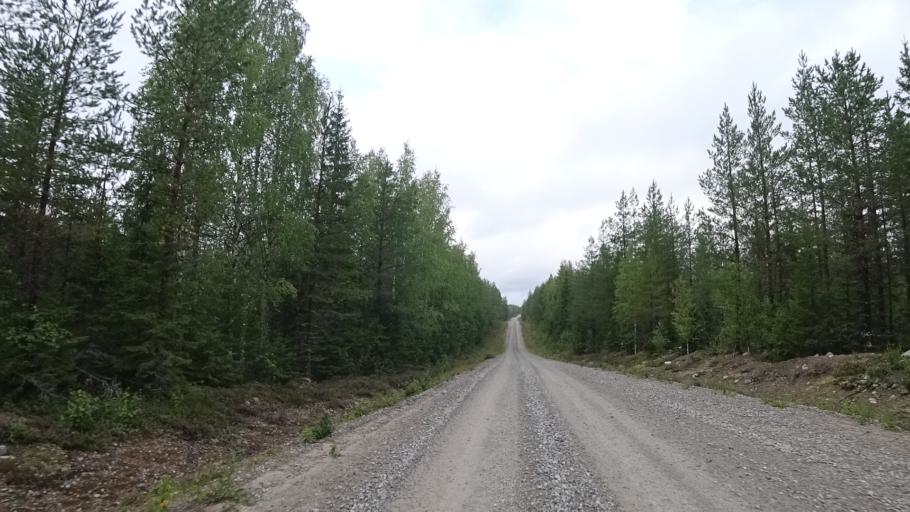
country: FI
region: North Karelia
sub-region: Pielisen Karjala
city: Lieksa
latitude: 63.4657
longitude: 30.2949
